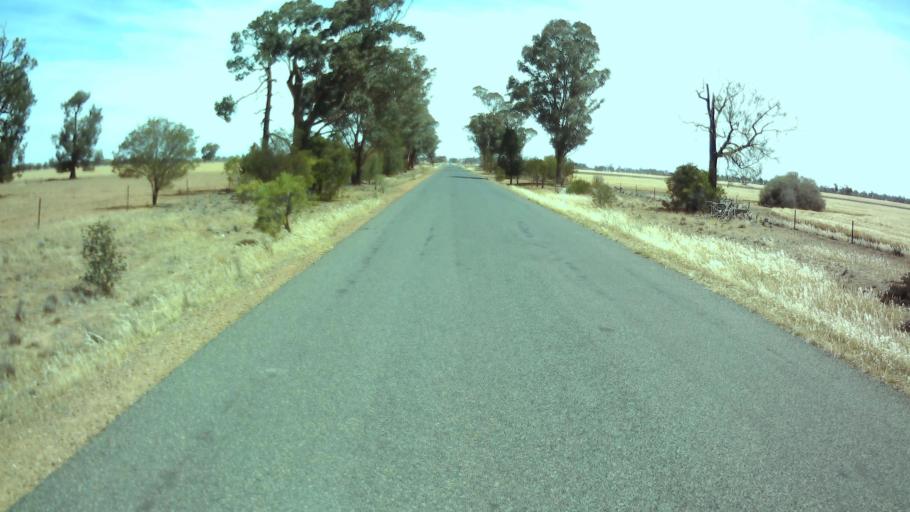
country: AU
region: New South Wales
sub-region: Weddin
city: Grenfell
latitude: -33.9802
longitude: 147.7781
